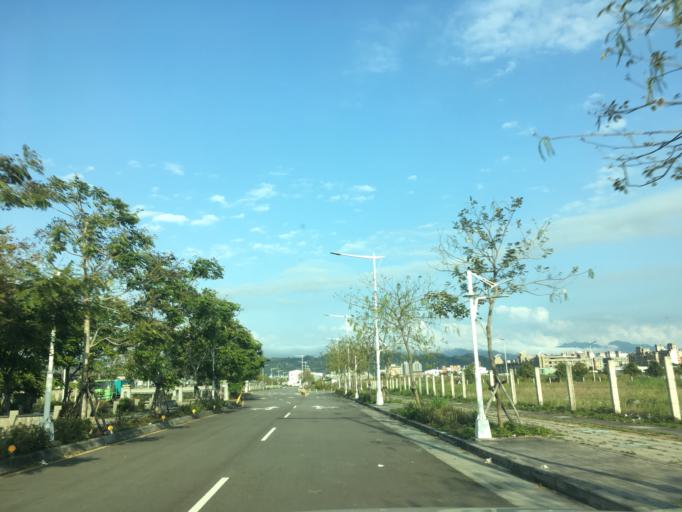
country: TW
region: Taiwan
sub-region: Taichung City
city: Taichung
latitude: 24.1993
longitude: 120.6894
